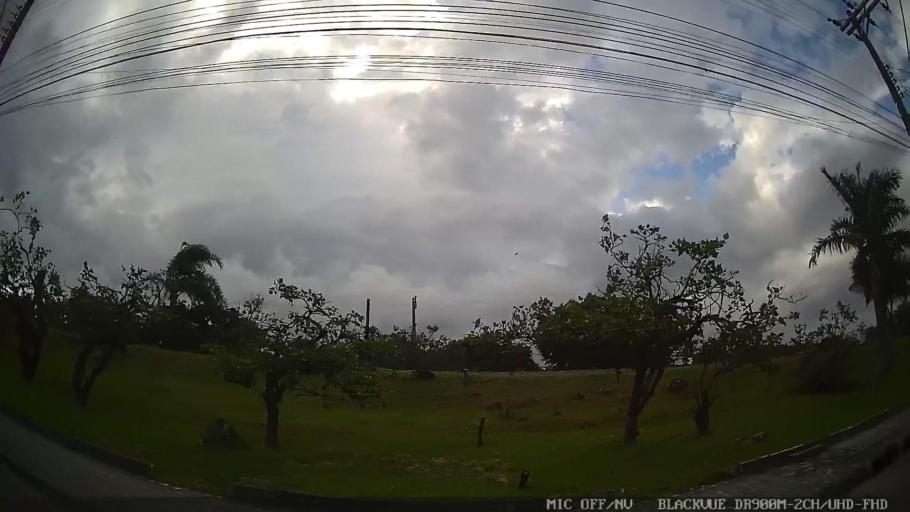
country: BR
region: Sao Paulo
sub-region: Itanhaem
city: Itanhaem
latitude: -24.1861
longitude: -46.7936
